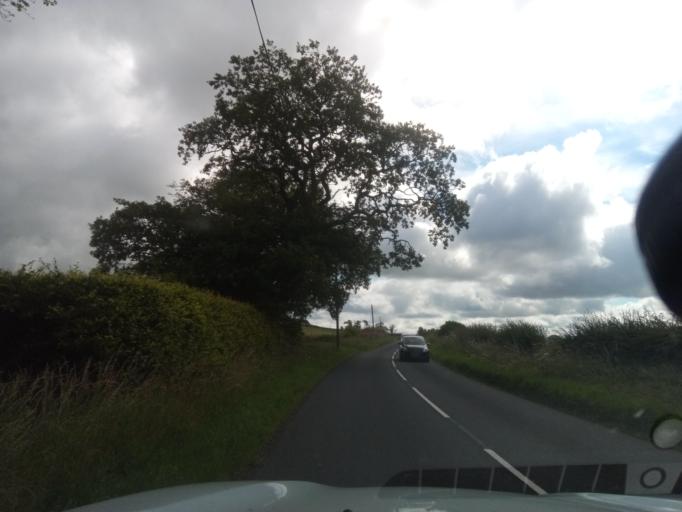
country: GB
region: Scotland
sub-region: The Scottish Borders
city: Saint Boswells
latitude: 55.6115
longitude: -2.6472
